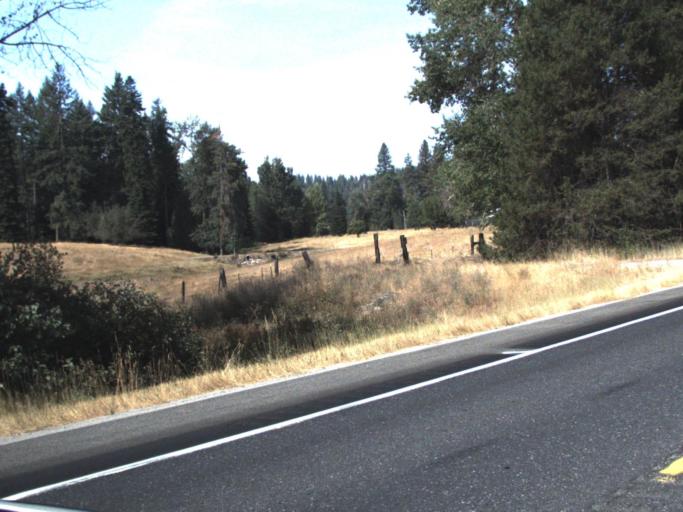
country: US
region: Washington
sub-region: Spokane County
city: Deer Park
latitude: 48.0169
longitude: -117.5879
